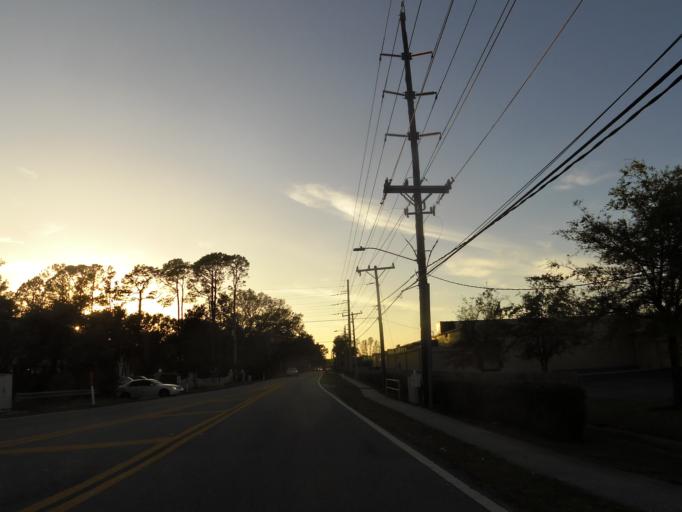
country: US
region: Florida
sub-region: Duval County
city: Jacksonville
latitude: 30.2863
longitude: -81.5798
